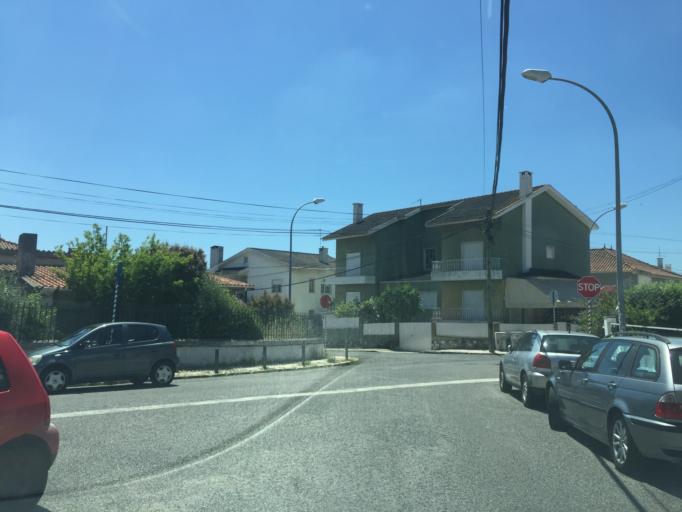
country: PT
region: Lisbon
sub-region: Oeiras
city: Quejas
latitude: 38.7223
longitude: -9.2628
